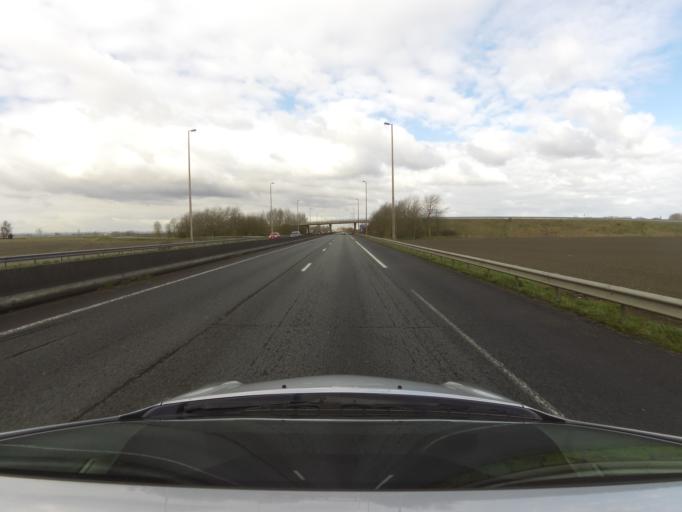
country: FR
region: Nord-Pas-de-Calais
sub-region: Departement du Pas-de-Calais
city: Marck
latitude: 50.9368
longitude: 1.9577
